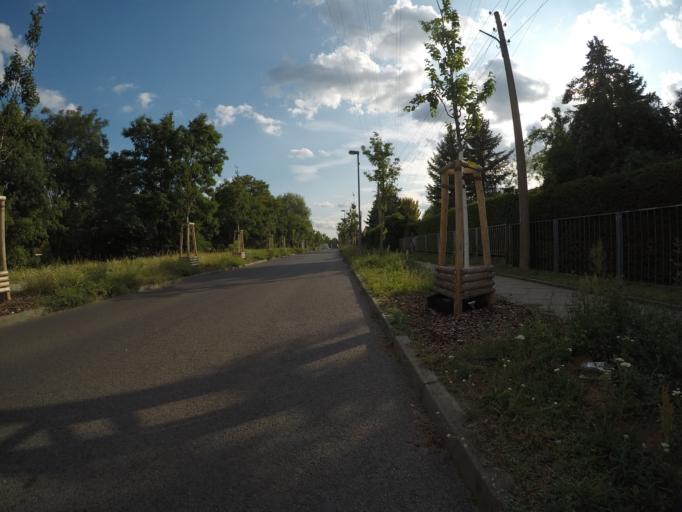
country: DE
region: Berlin
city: Kaulsdorf
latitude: 52.5204
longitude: 13.5979
